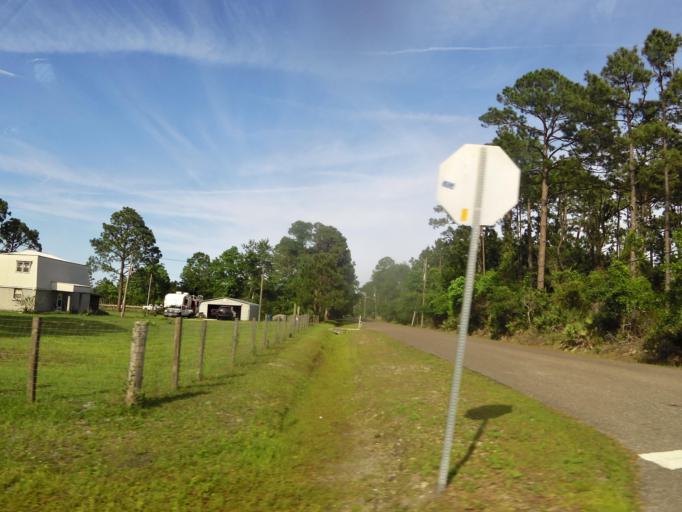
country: US
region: Florida
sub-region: Nassau County
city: Fernandina Beach
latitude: 30.5141
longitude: -81.4777
